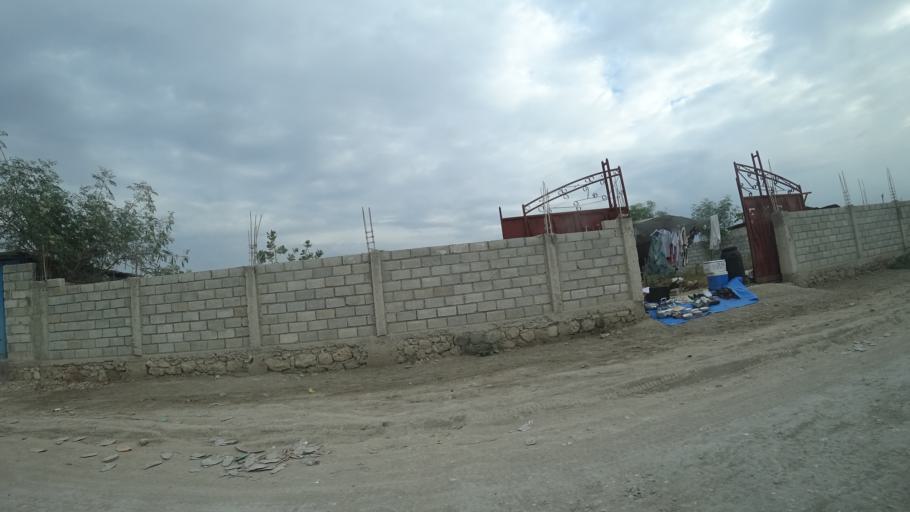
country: HT
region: Ouest
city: Croix des Bouquets
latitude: 18.6512
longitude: -72.2561
